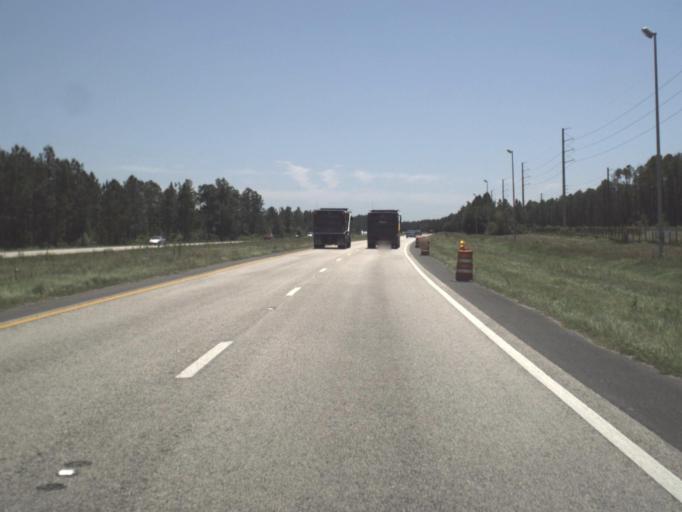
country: US
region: Florida
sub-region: Clay County
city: Bellair-Meadowbrook Terrace
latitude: 30.2415
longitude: -81.8442
